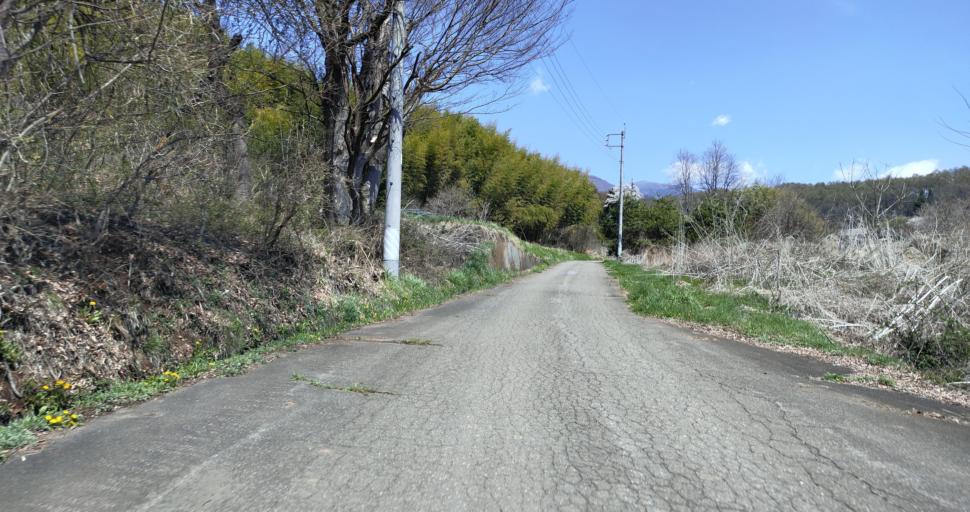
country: JP
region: Nagano
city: Komoro
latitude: 36.3633
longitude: 138.3983
